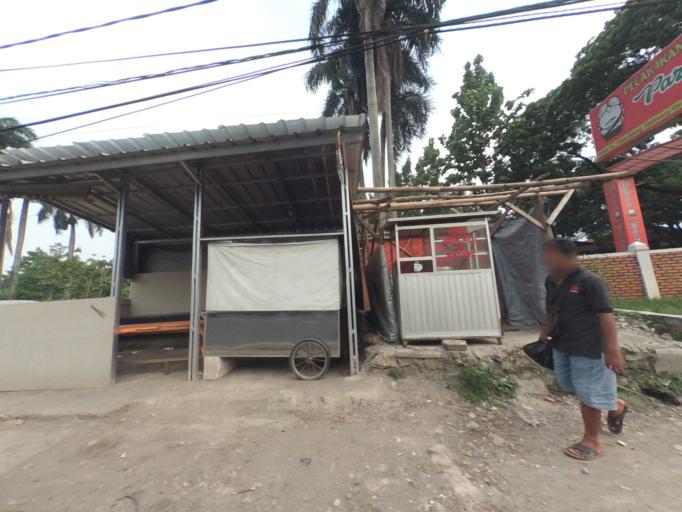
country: ID
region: West Java
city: Ciampea
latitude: -6.5562
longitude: 106.6955
